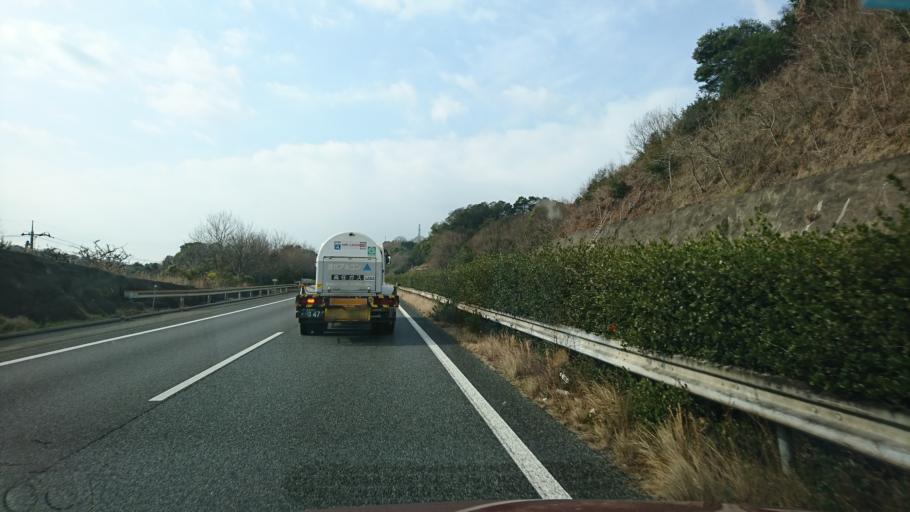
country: JP
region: Okayama
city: Kurashiki
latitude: 34.5792
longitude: 133.6765
